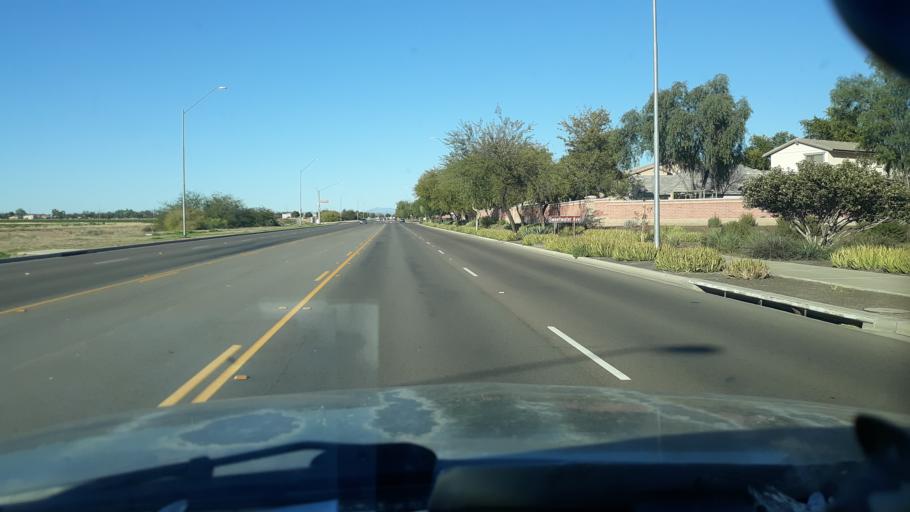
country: US
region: Arizona
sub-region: Maricopa County
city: Surprise
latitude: 33.6003
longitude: -112.3938
